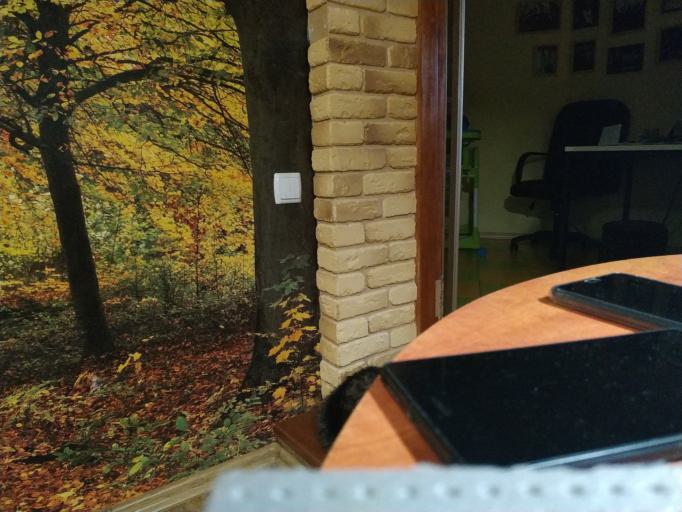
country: RU
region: Tverskaya
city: Zubtsov
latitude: 56.3703
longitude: 34.6609
